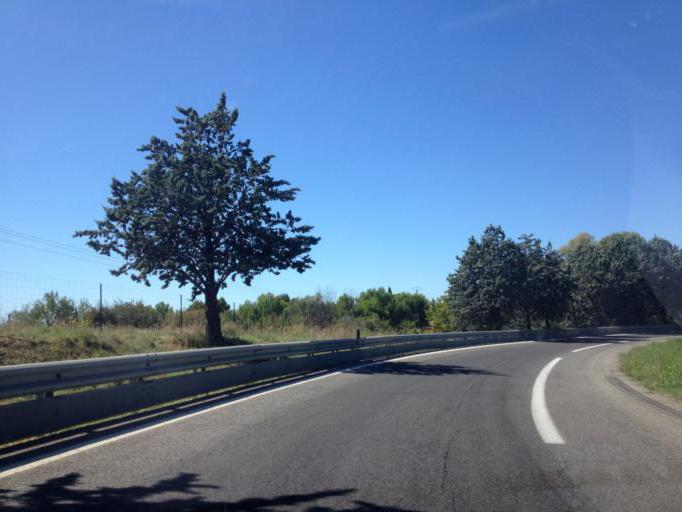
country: FR
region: Provence-Alpes-Cote d'Azur
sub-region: Departement des Bouches-du-Rhone
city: Aix-en-Provence
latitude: 43.5254
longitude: 5.4025
